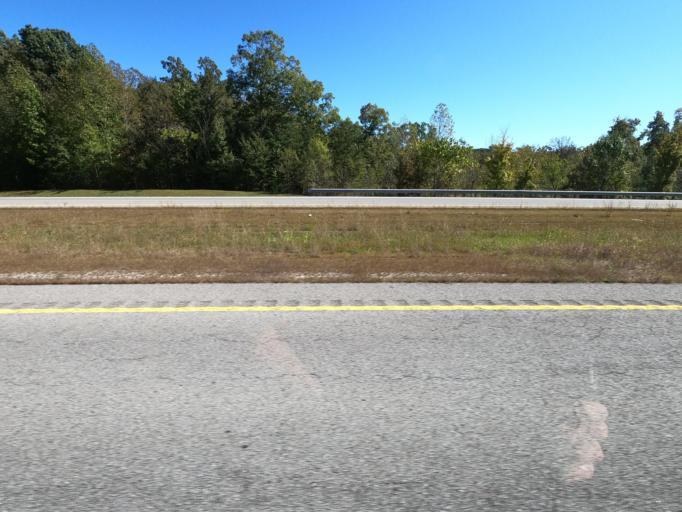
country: US
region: Tennessee
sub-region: Maury County
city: Mount Pleasant
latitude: 35.4644
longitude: -87.2670
